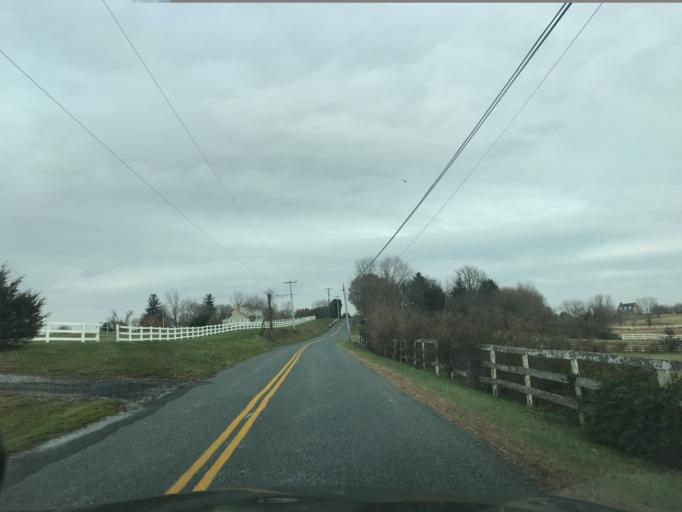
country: US
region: Maryland
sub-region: Harford County
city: Jarrettsville
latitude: 39.6787
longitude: -76.4282
